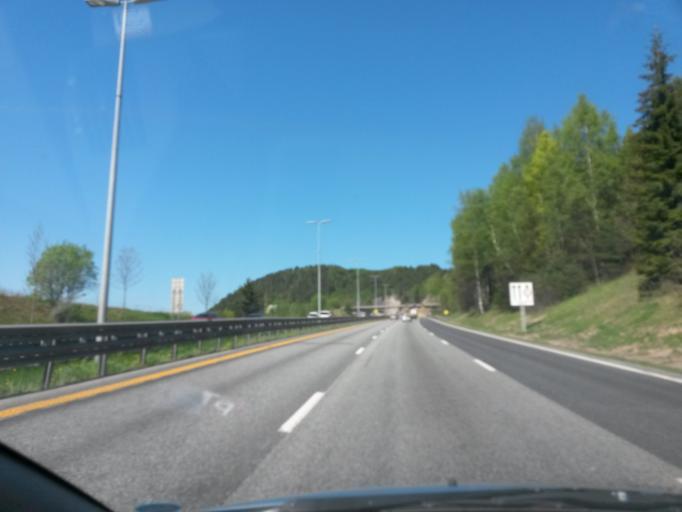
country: NO
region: Buskerud
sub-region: Lier
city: Tranby
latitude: 59.7853
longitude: 10.2731
